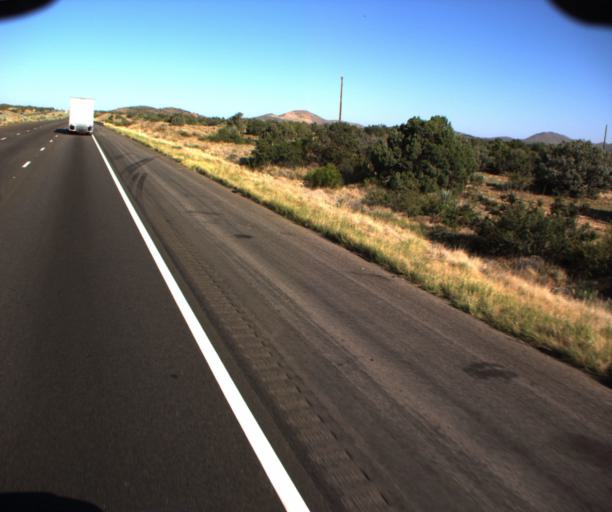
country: US
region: Arizona
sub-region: Mohave County
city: New Kingman-Butler
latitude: 35.1668
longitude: -113.7455
